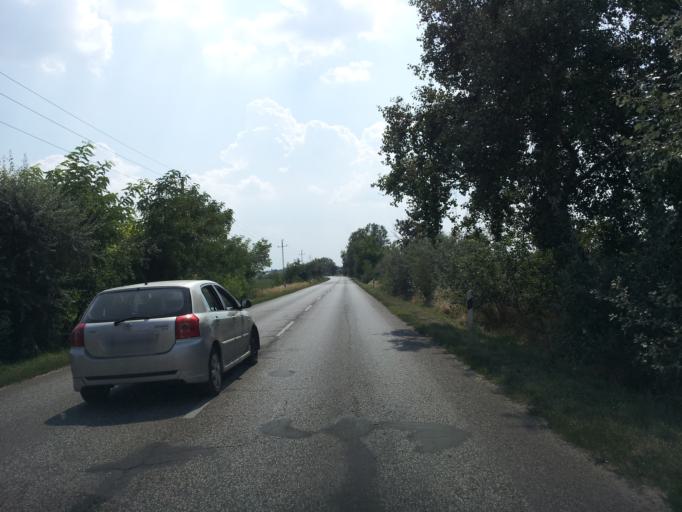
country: HU
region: Pest
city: Taksony
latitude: 47.3194
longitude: 19.0470
